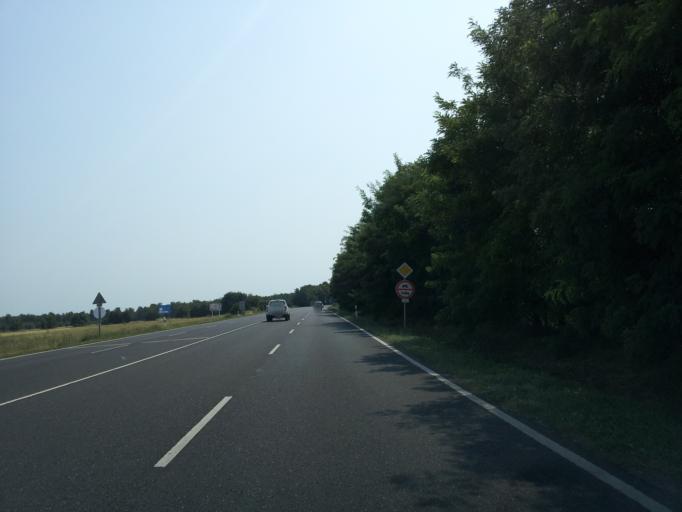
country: HU
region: Veszprem
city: Veszprem
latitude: 47.0610
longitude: 17.9248
